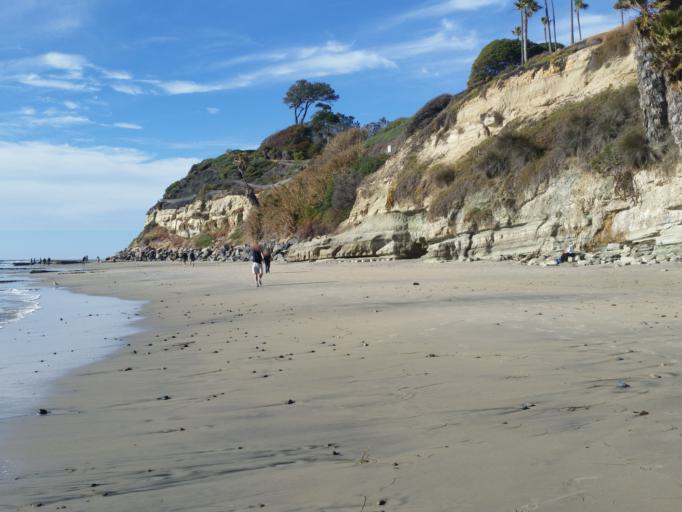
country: US
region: California
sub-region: San Diego County
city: Encinitas
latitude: 33.0343
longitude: -117.2922
